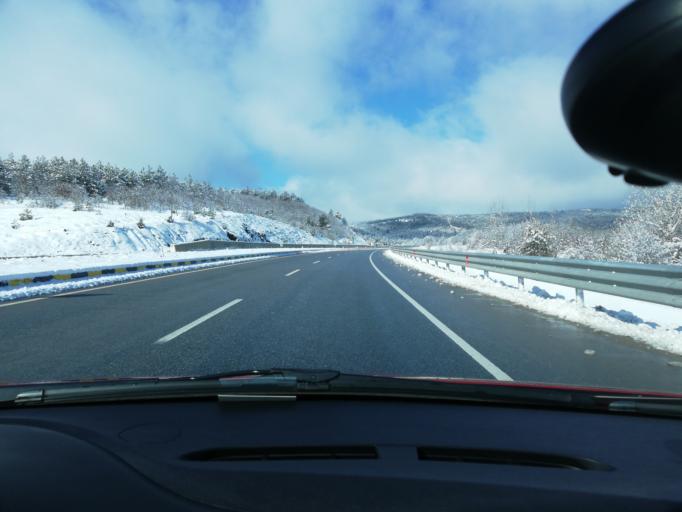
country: TR
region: Kastamonu
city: Kuzyaka
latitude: 41.3358
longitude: 33.6374
